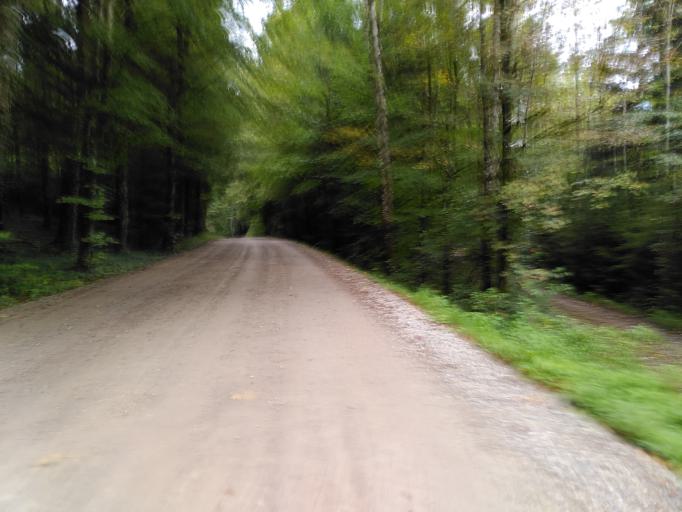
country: CH
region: Bern
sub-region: Emmental District
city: Ersigen
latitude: 47.0961
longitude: 7.6261
